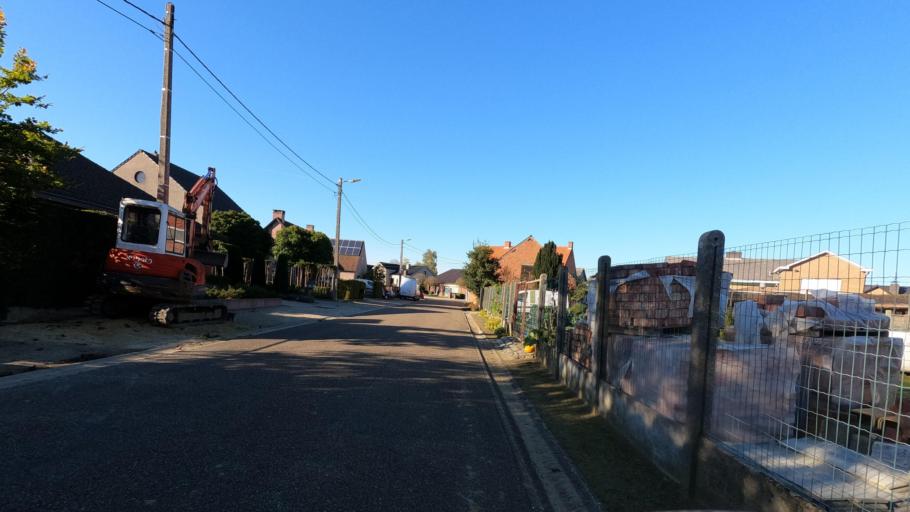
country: BE
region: Flanders
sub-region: Provincie Antwerpen
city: Hulshout
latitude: 51.1068
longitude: 4.7852
